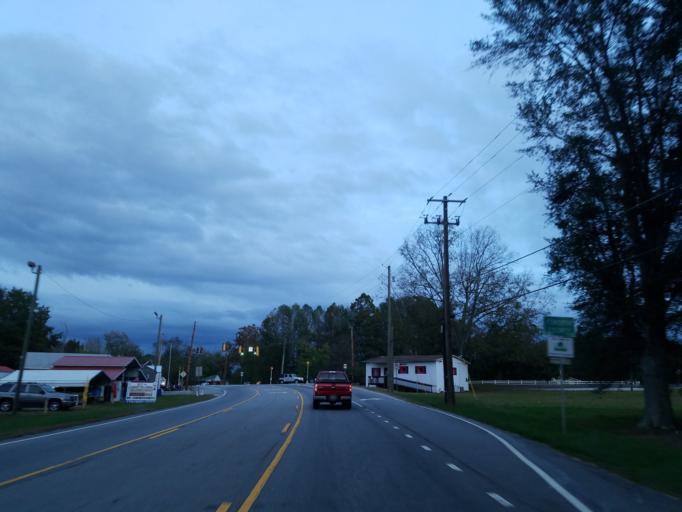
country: US
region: Georgia
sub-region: Dawson County
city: Dawsonville
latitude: 34.3347
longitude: -84.1174
